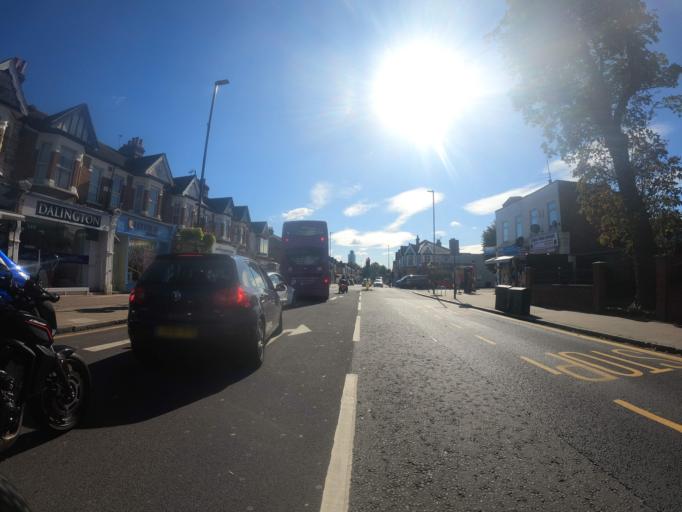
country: GB
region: England
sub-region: Greater London
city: Brentford
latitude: 51.4987
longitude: -0.3060
